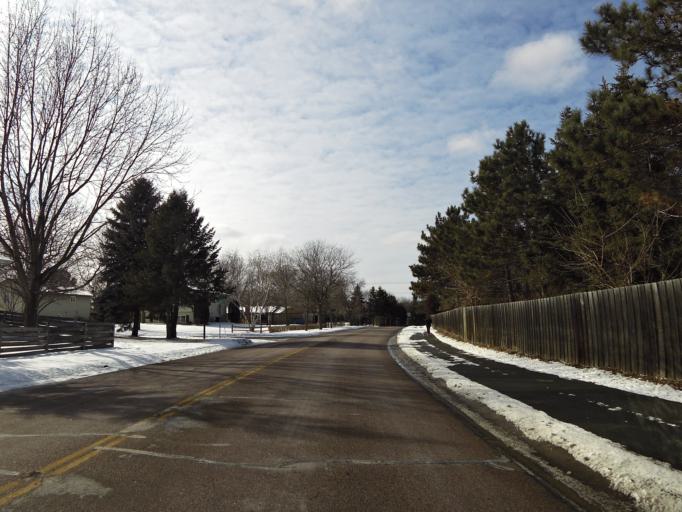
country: US
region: Minnesota
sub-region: Hennepin County
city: Eden Prairie
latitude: 44.8170
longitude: -93.4252
